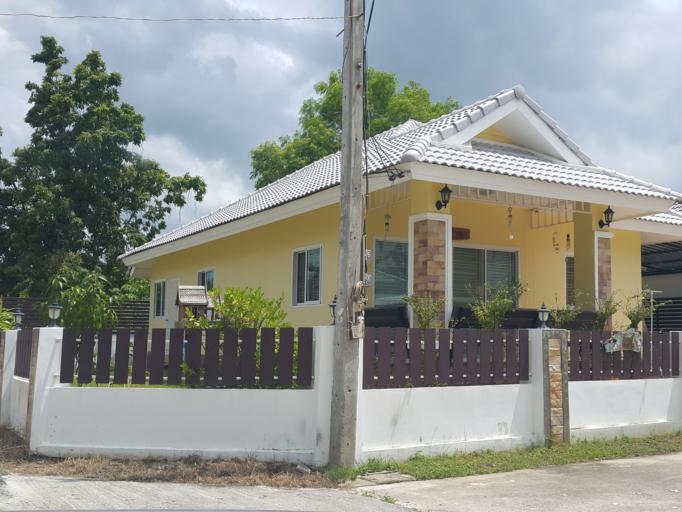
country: TH
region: Chiang Mai
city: San Kamphaeng
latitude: 18.7932
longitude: 99.1088
